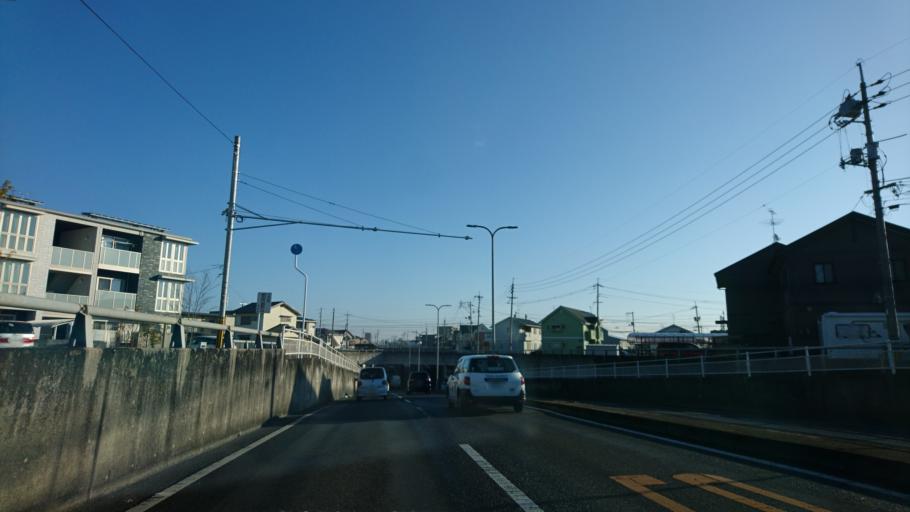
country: JP
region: Okayama
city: Kurashiki
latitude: 34.6059
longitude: 133.7553
